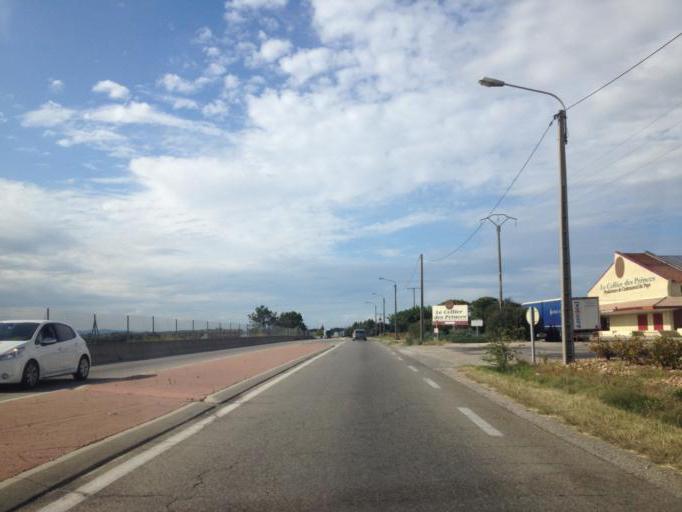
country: FR
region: Provence-Alpes-Cote d'Azur
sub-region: Departement du Vaucluse
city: Courthezon
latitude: 44.0955
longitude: 4.8724
